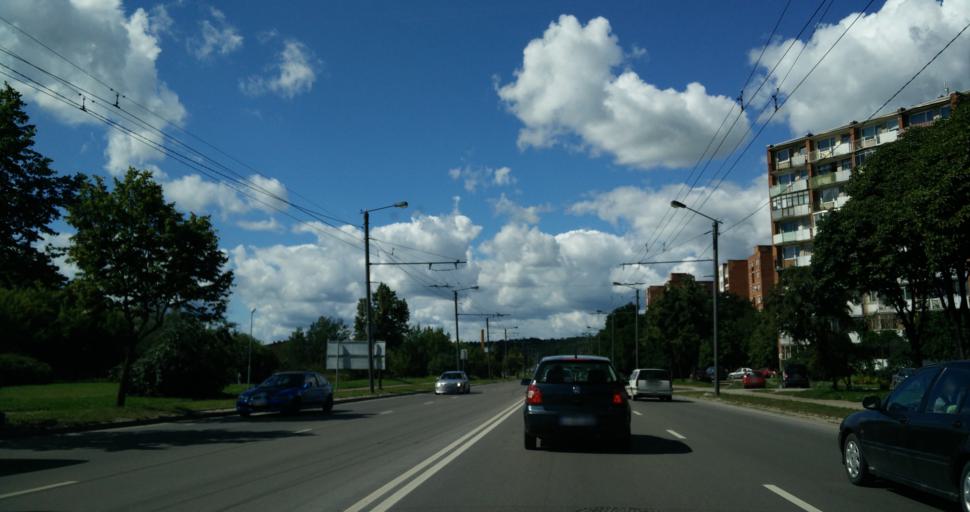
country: LT
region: Kauno apskritis
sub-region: Kauno rajonas
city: Akademija (Kaunas)
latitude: 54.9168
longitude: 23.8345
